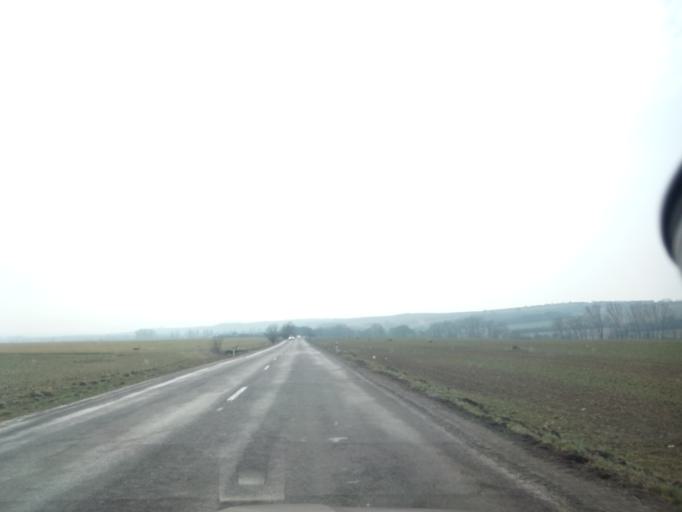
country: SK
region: Kosicky
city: Secovce
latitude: 48.6334
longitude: 21.5832
